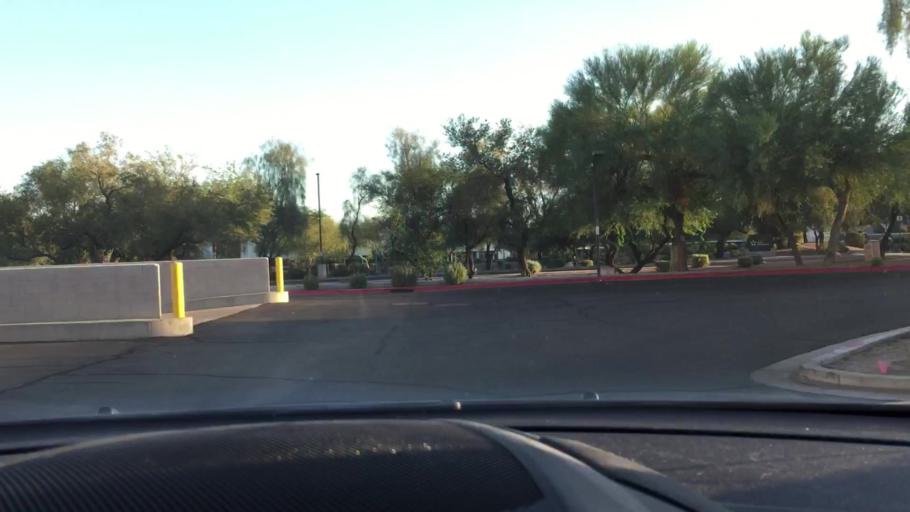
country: US
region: Arizona
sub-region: Maricopa County
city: Guadalupe
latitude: 33.3169
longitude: -111.9759
